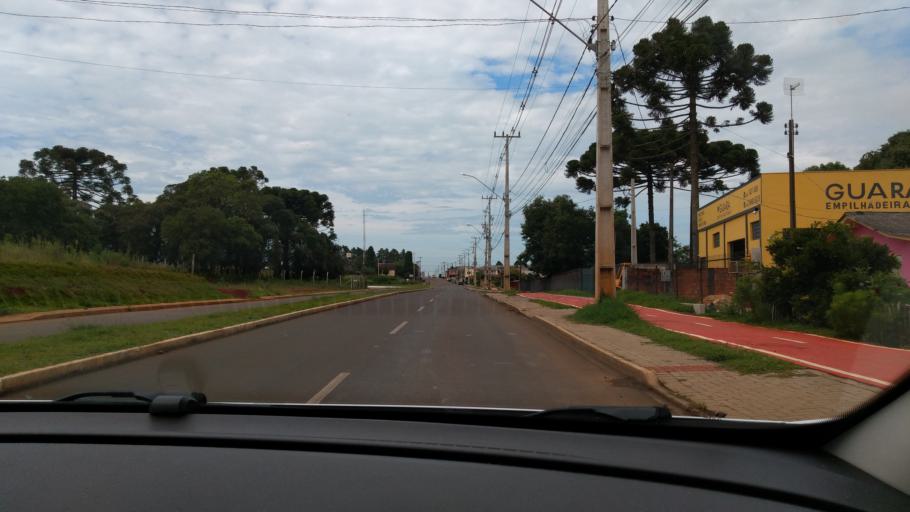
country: BR
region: Parana
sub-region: Guarapuava
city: Guarapuava
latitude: -25.3704
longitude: -51.4403
